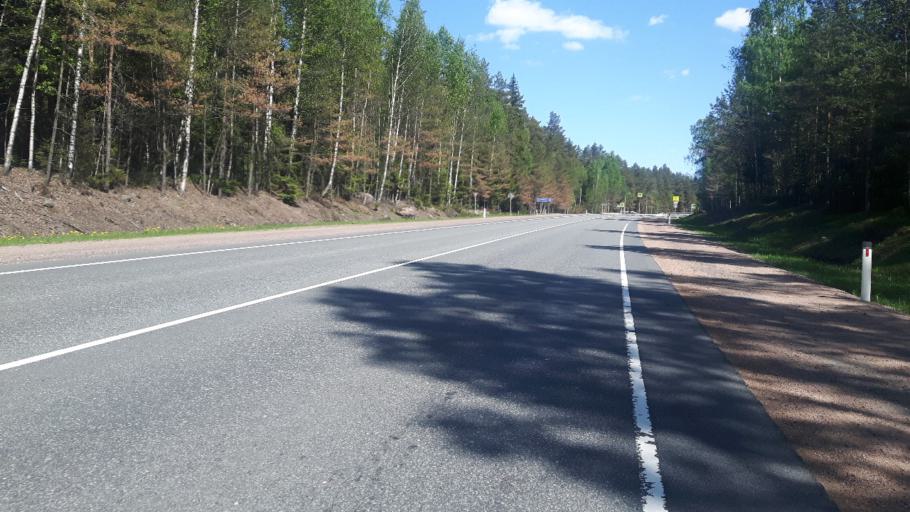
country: RU
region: Leningrad
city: Vysotsk
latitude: 60.6361
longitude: 28.2798
